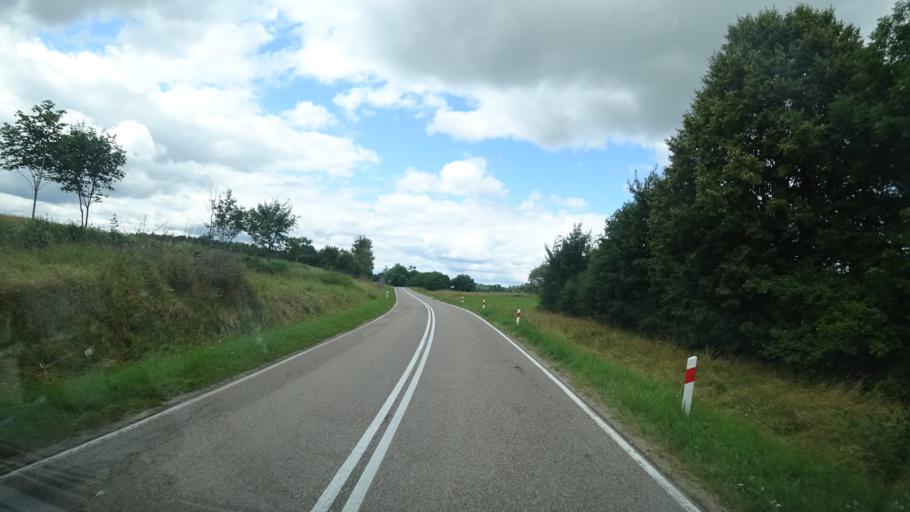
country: PL
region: Warmian-Masurian Voivodeship
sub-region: Powiat goldapski
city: Banie Mazurskie
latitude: 54.2094
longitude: 22.1835
